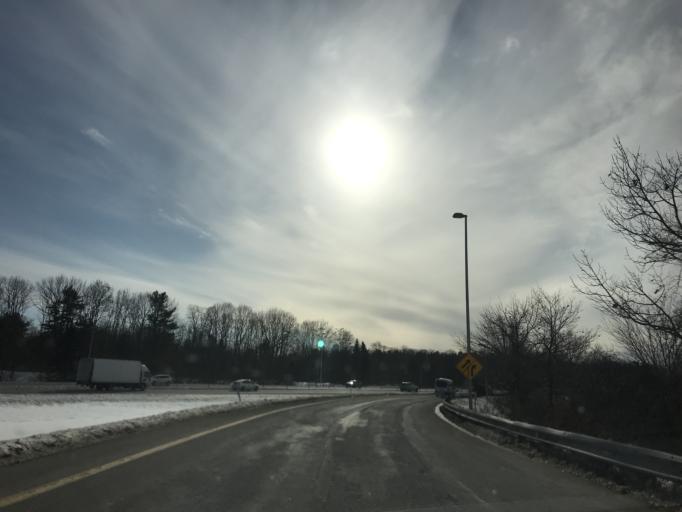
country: US
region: Maine
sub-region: Cumberland County
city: South Portland Gardens
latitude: 43.6379
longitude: -70.2969
